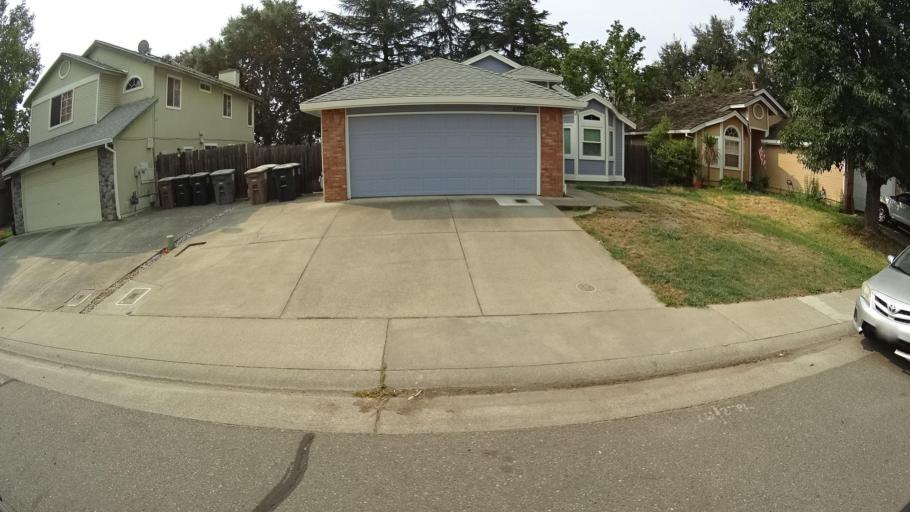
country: US
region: California
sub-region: Sacramento County
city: Laguna
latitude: 38.4098
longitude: -121.4002
